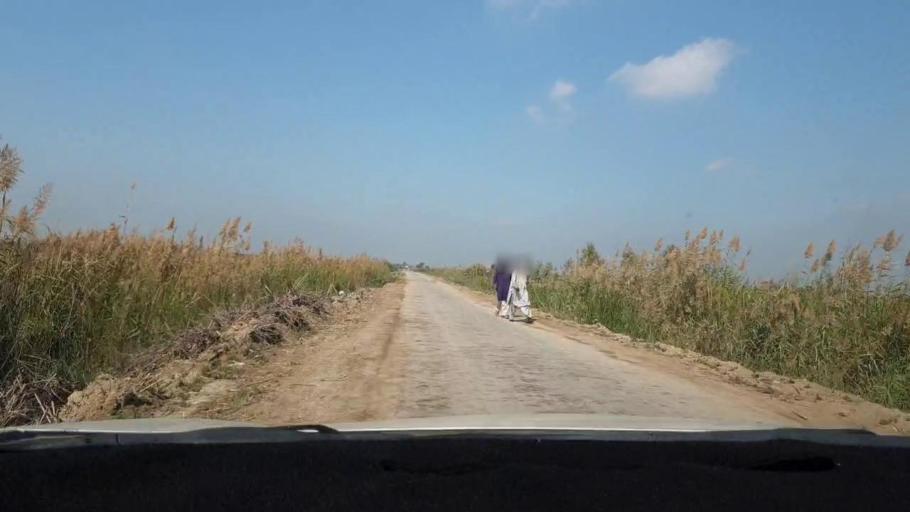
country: PK
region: Sindh
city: Berani
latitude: 25.7934
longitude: 68.8369
